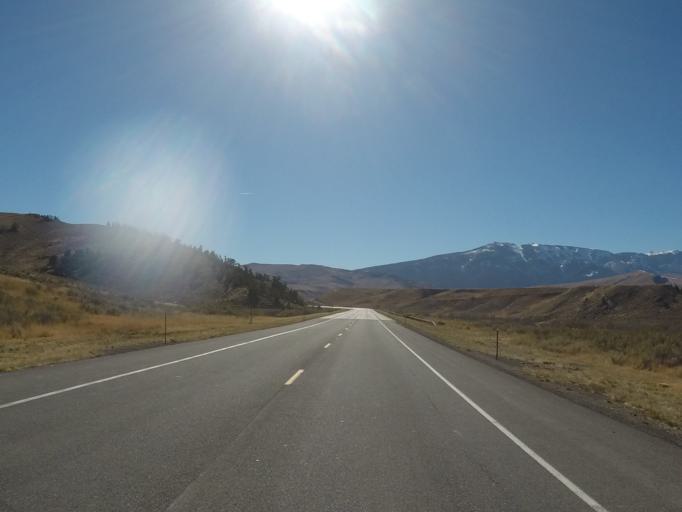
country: US
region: Wyoming
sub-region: Park County
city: Cody
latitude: 44.7390
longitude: -109.2136
